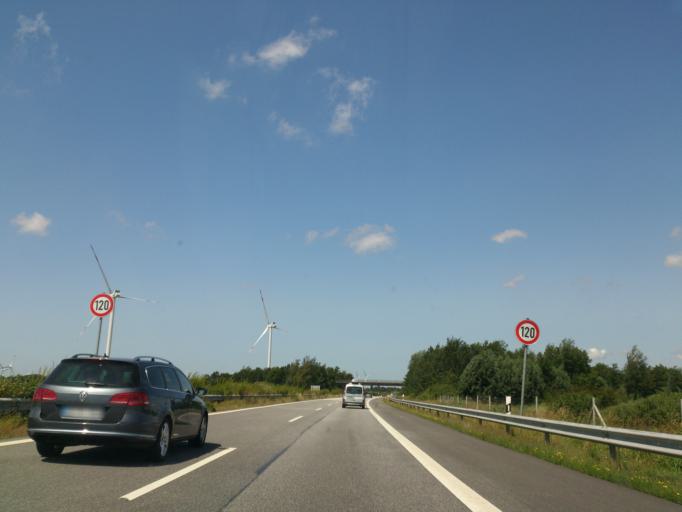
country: DE
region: Schleswig-Holstein
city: Lohe-Rickelshof
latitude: 54.1794
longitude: 9.0553
